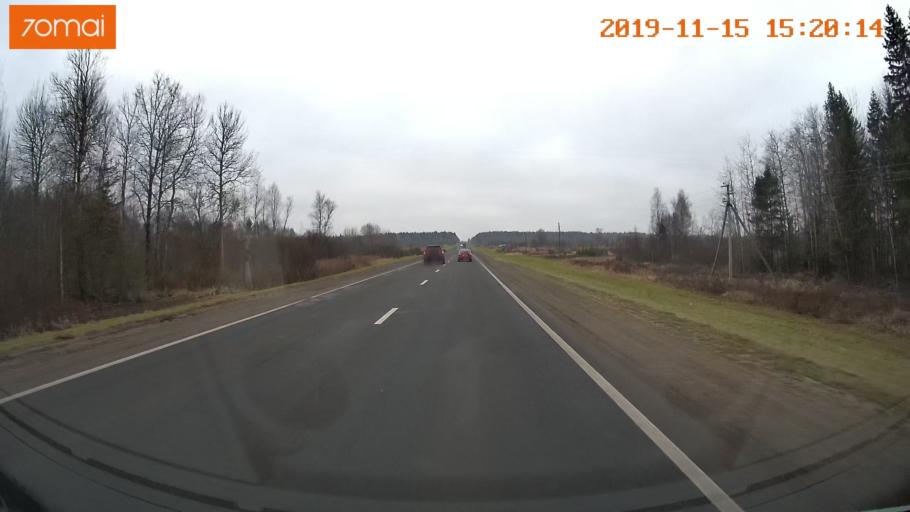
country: RU
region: Jaroslavl
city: Danilov
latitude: 58.2258
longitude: 40.1651
